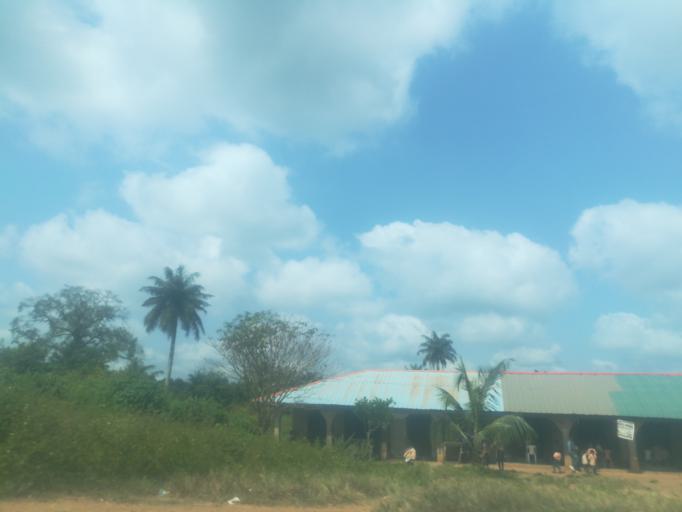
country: NG
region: Oyo
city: Moniya
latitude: 7.5851
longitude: 3.9114
